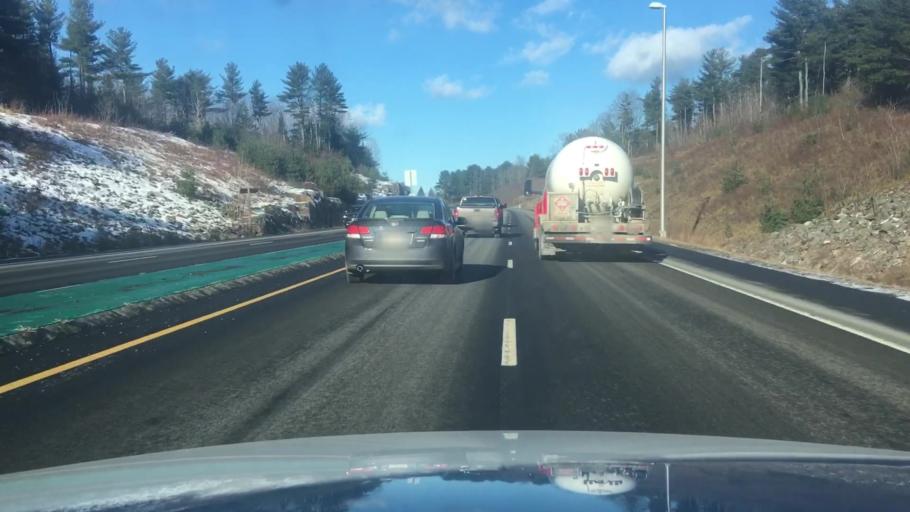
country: US
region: Maine
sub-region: Kennebec County
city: Augusta
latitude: 44.3473
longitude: -69.7720
